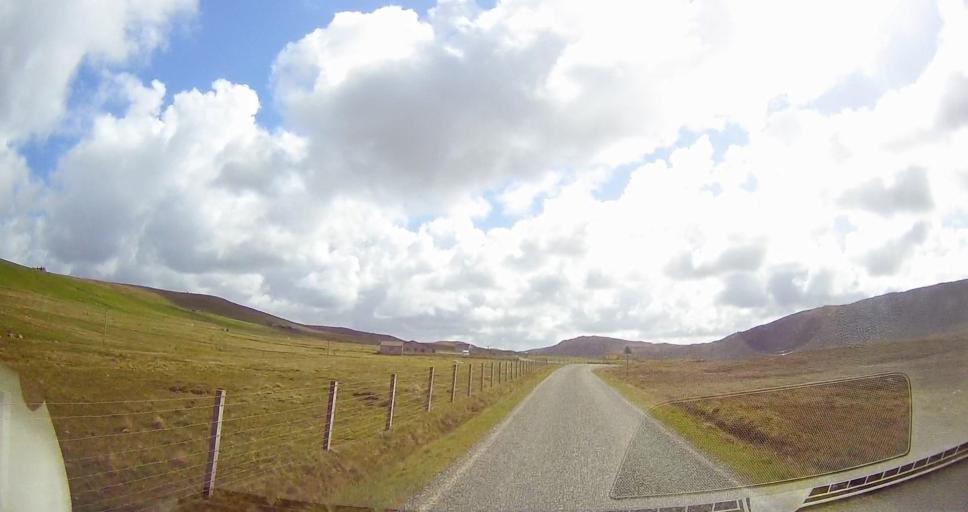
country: GB
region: Scotland
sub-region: Shetland Islands
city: Lerwick
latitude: 60.5737
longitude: -1.3314
